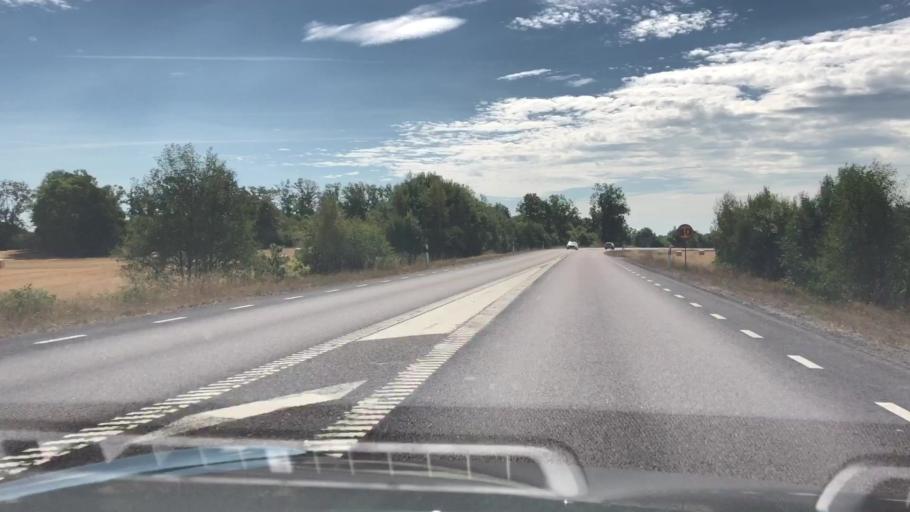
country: SE
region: Kalmar
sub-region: Torsas Kommun
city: Torsas
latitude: 56.4330
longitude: 16.0766
